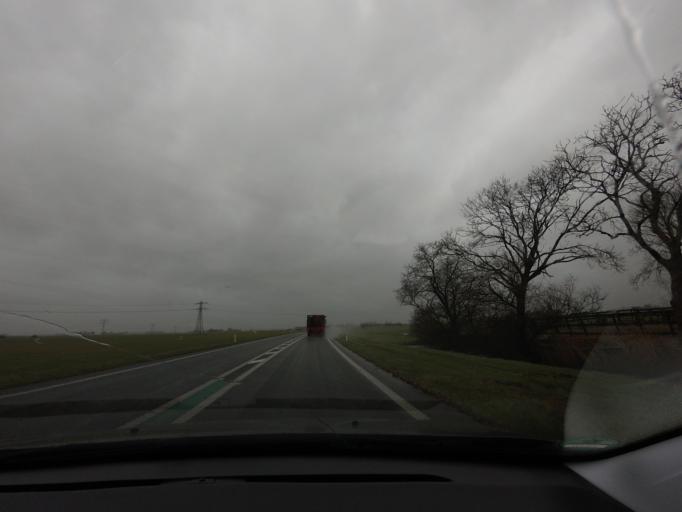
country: NL
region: Friesland
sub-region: Sudwest Fryslan
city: Bolsward
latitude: 53.0736
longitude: 5.5108
